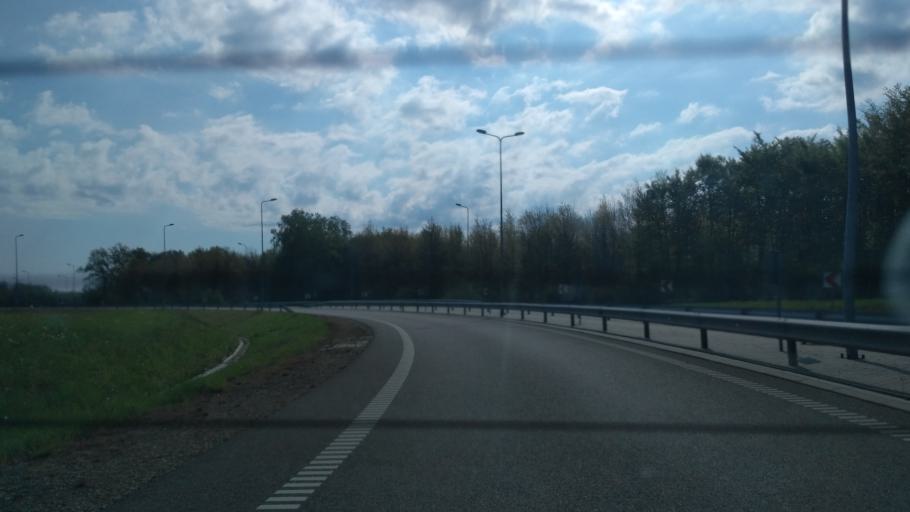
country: PL
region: Subcarpathian Voivodeship
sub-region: Powiat lubaczowski
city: Wielkie Oczy
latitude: 49.9614
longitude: 23.0716
